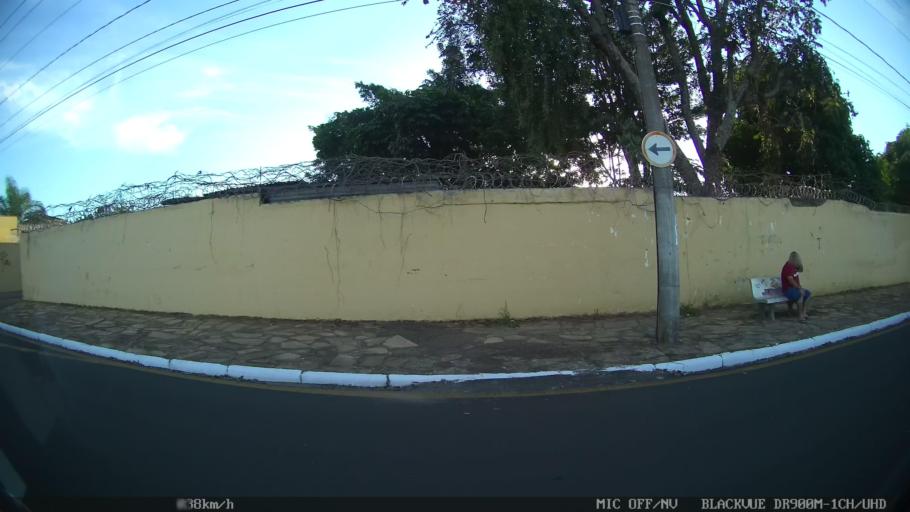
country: BR
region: Sao Paulo
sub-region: Franca
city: Franca
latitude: -20.5245
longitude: -47.3954
